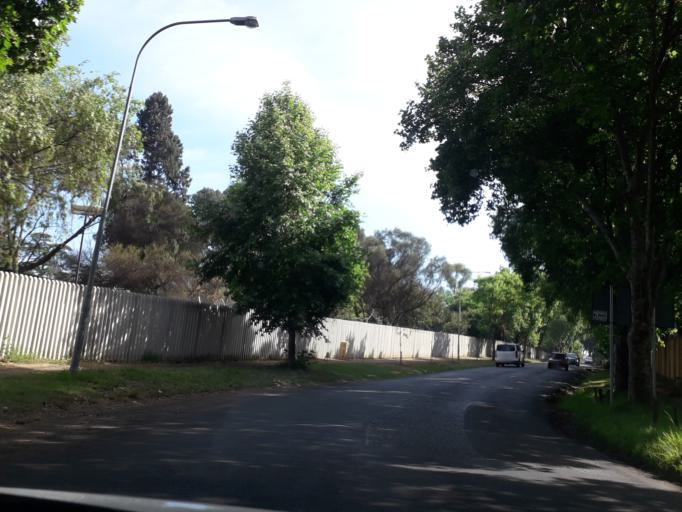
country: ZA
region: Gauteng
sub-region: City of Johannesburg Metropolitan Municipality
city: Johannesburg
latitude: -26.1678
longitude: 28.0410
